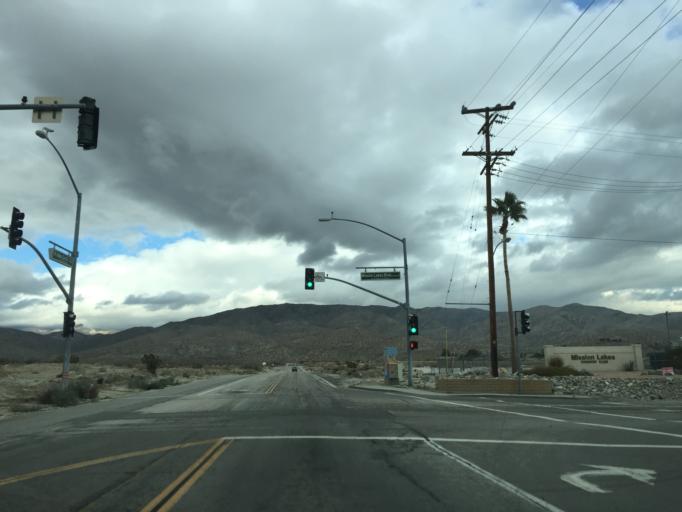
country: US
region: California
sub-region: Riverside County
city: Desert Hot Springs
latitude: 33.9759
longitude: -116.5449
